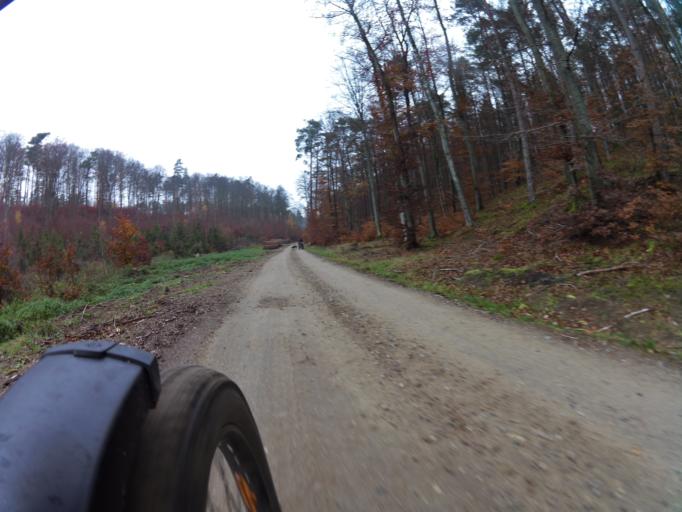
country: PL
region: Pomeranian Voivodeship
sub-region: Powiat wejherowski
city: Orle
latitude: 54.7034
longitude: 18.1455
